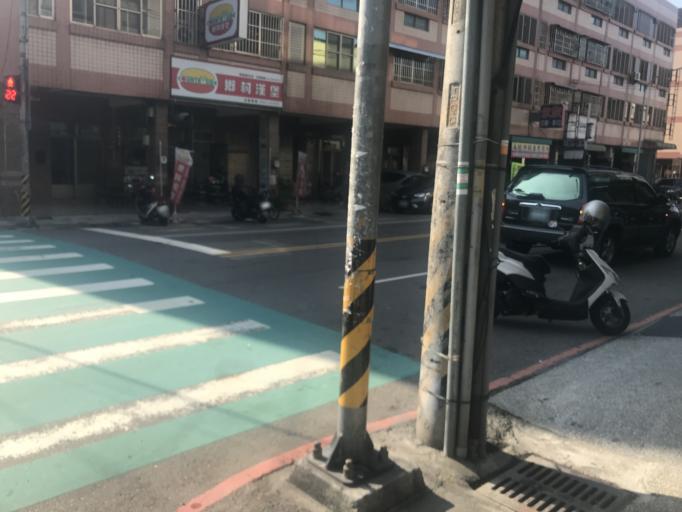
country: TW
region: Taiwan
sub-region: Taichung City
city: Taichung
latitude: 24.1109
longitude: 120.6577
